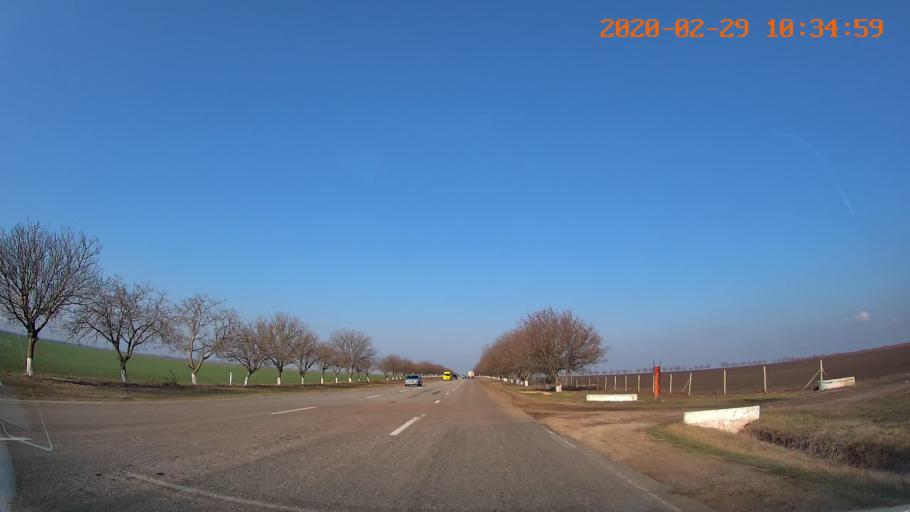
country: MD
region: Anenii Noi
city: Varnita
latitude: 46.9815
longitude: 29.5270
